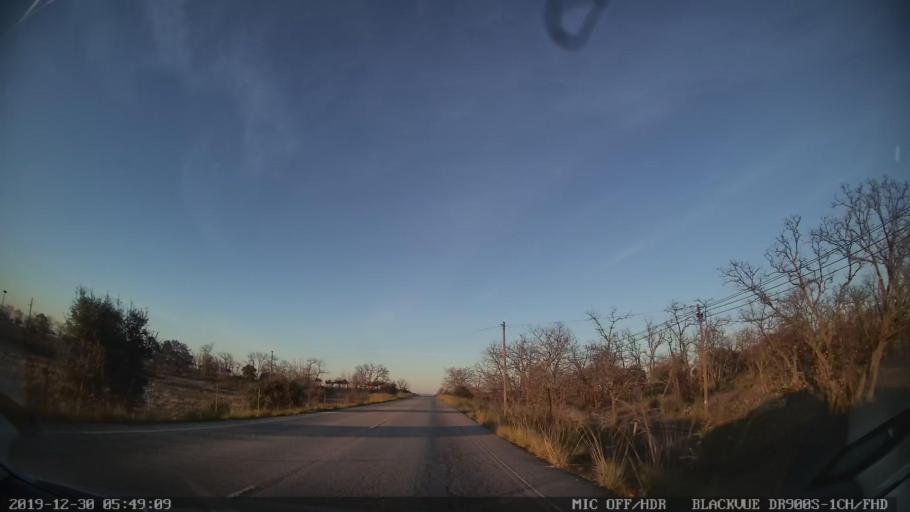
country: PT
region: Castelo Branco
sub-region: Idanha-A-Nova
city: Idanha-a-Nova
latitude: 39.9710
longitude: -7.2428
